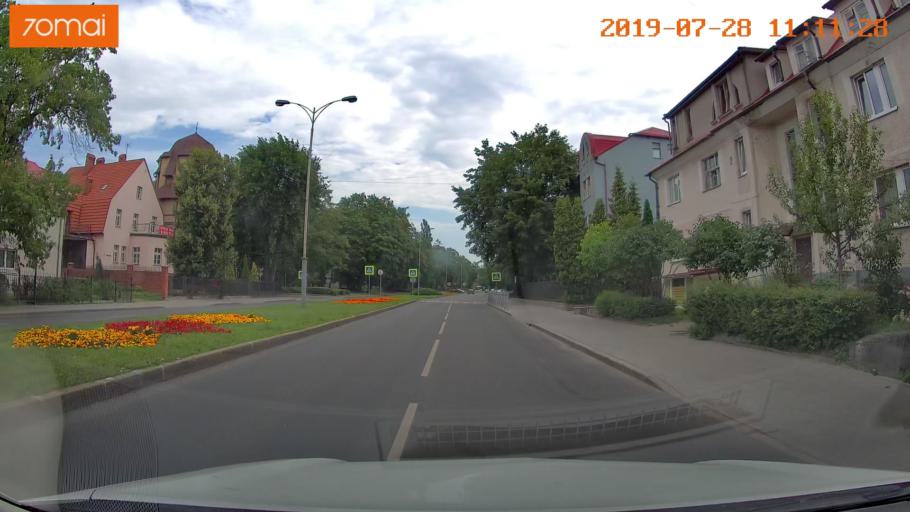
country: RU
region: Kaliningrad
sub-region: Gorod Kaliningrad
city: Kaliningrad
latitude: 54.7156
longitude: 20.4612
